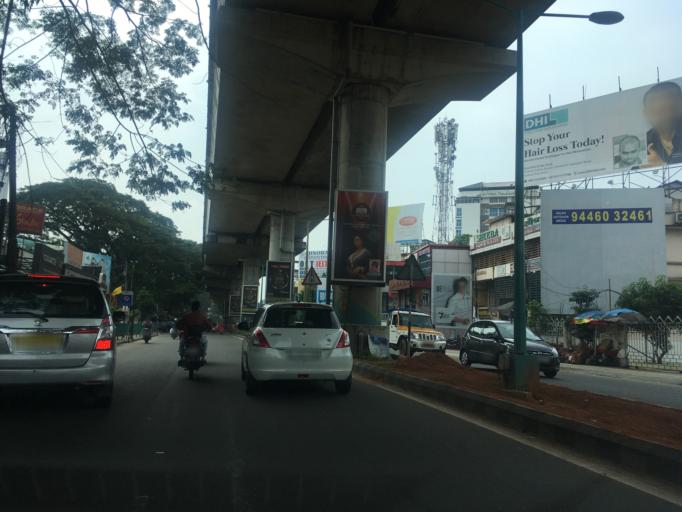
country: IN
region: Kerala
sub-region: Ernakulam
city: Elur
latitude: 10.0214
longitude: 76.3066
